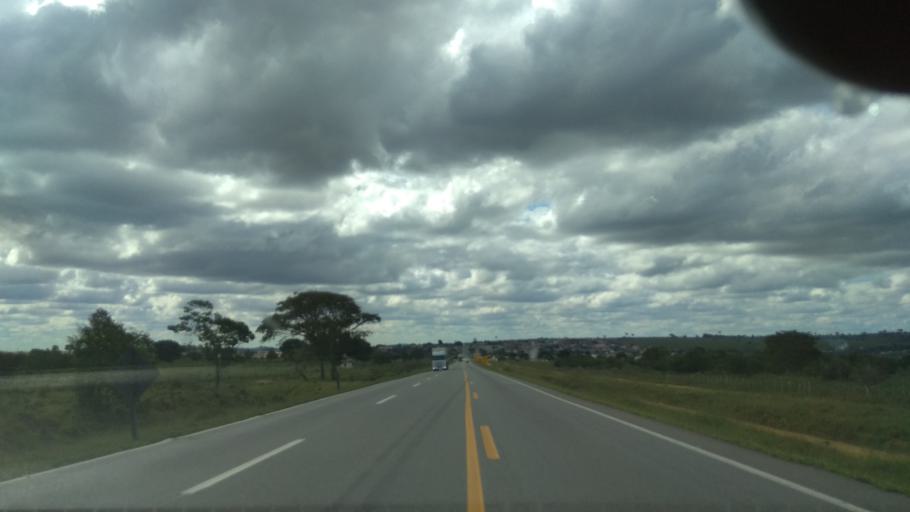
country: BR
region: Bahia
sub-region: Santa Ines
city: Santa Ines
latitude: -13.0898
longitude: -39.9628
